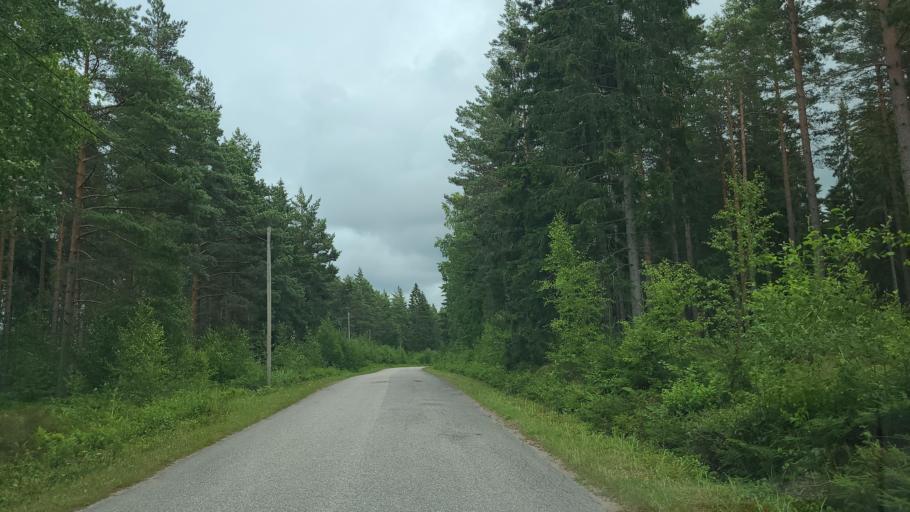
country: FI
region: Varsinais-Suomi
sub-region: Aboland-Turunmaa
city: Dragsfjaerd
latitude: 60.0800
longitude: 22.4205
